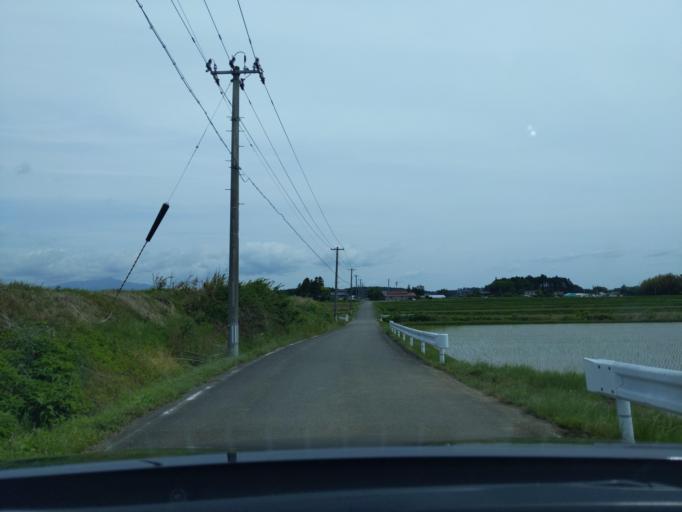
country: JP
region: Fukushima
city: Koriyama
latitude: 37.3800
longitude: 140.2902
